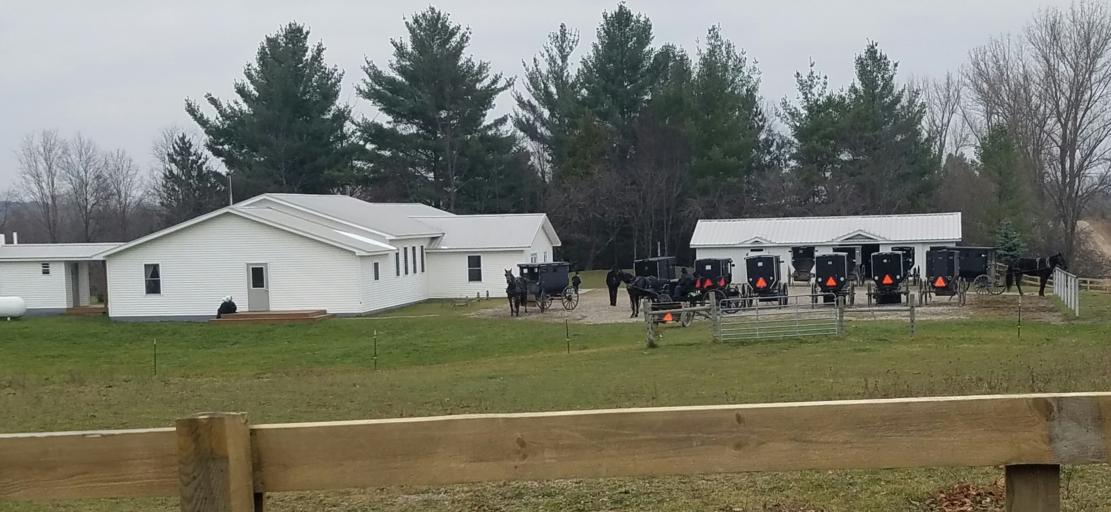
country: US
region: Michigan
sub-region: Wexford County
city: Manton
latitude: 44.4063
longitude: -85.4797
